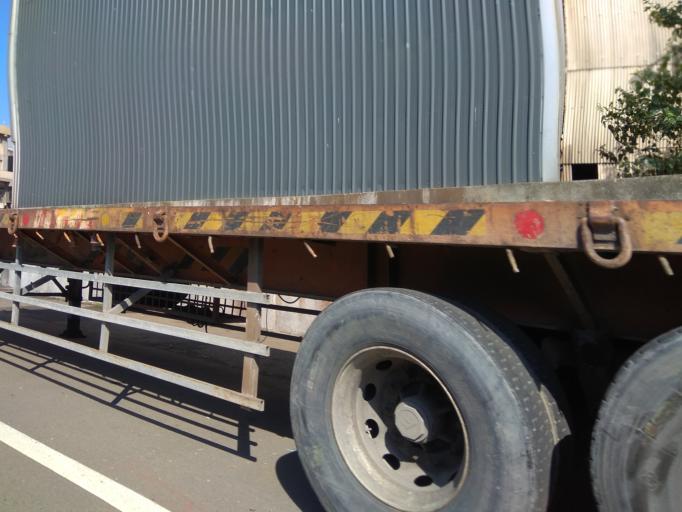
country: TW
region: Taiwan
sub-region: Hsinchu
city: Zhubei
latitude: 24.9802
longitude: 121.0385
